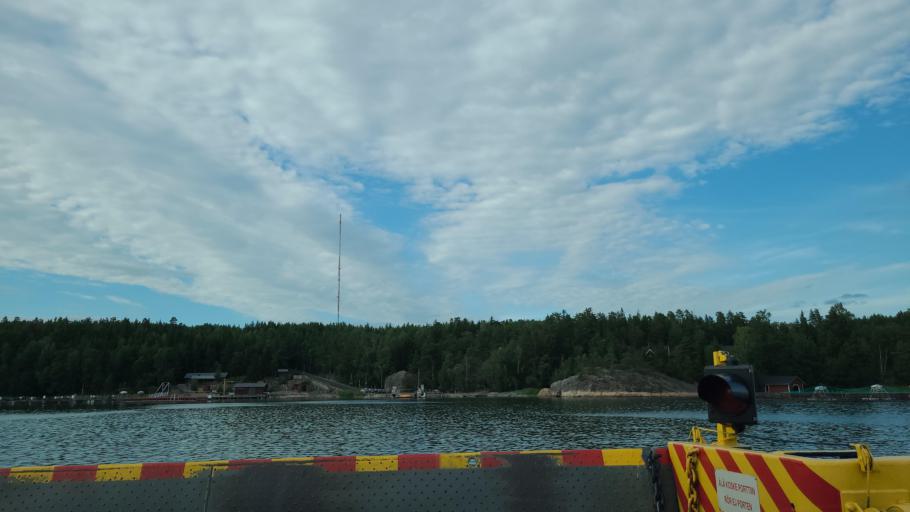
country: FI
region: Varsinais-Suomi
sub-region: Turku
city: Rymaettylae
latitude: 60.3144
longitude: 21.9620
